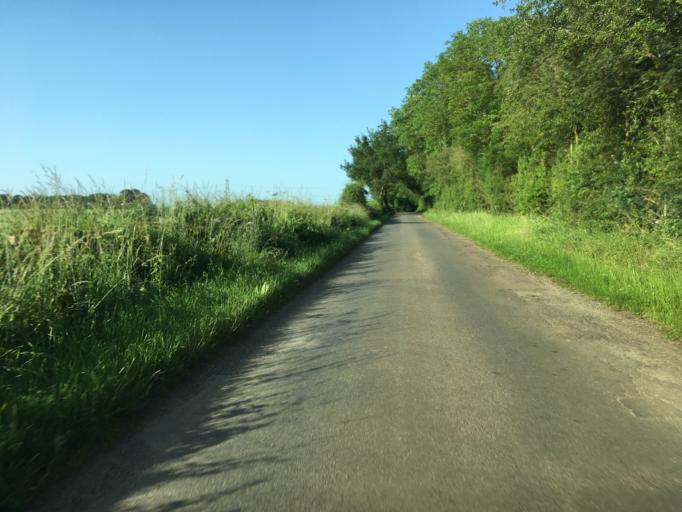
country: GB
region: England
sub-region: Gloucestershire
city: Lechlade
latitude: 51.7669
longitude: -1.7156
